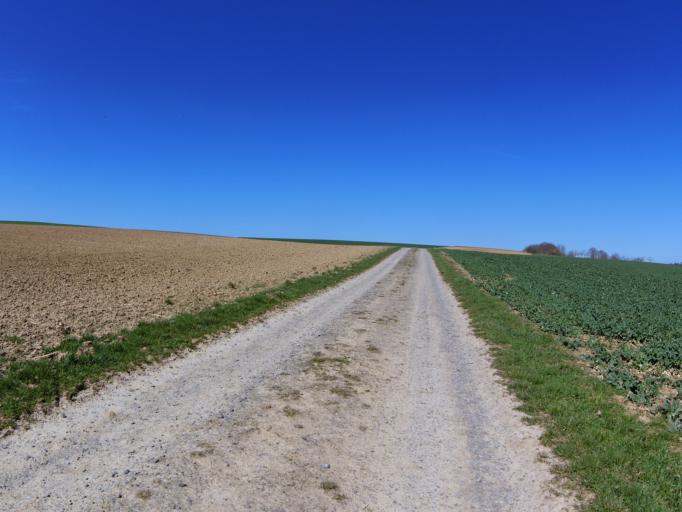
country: DE
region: Bavaria
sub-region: Regierungsbezirk Unterfranken
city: Prosselsheim
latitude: 49.8489
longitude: 10.1382
